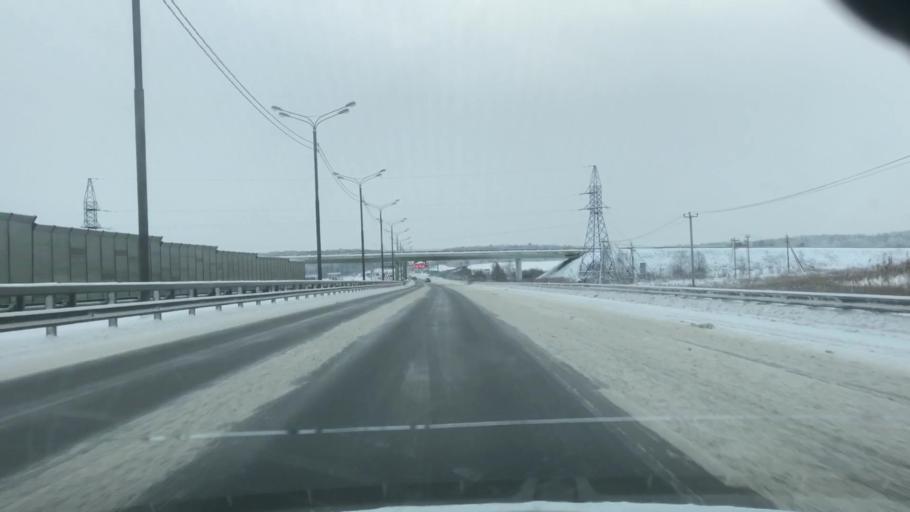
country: RU
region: Moskovskaya
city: Mikhnevo
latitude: 55.1887
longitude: 37.8974
